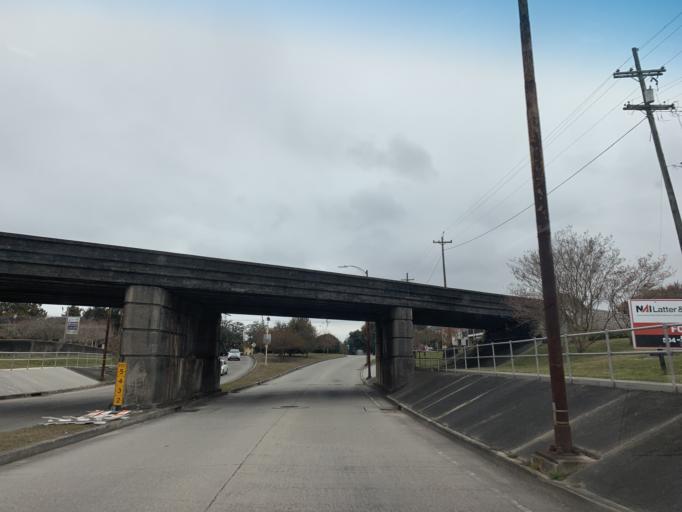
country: US
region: Louisiana
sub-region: Jefferson Parish
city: Metairie
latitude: 29.9915
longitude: -90.1096
